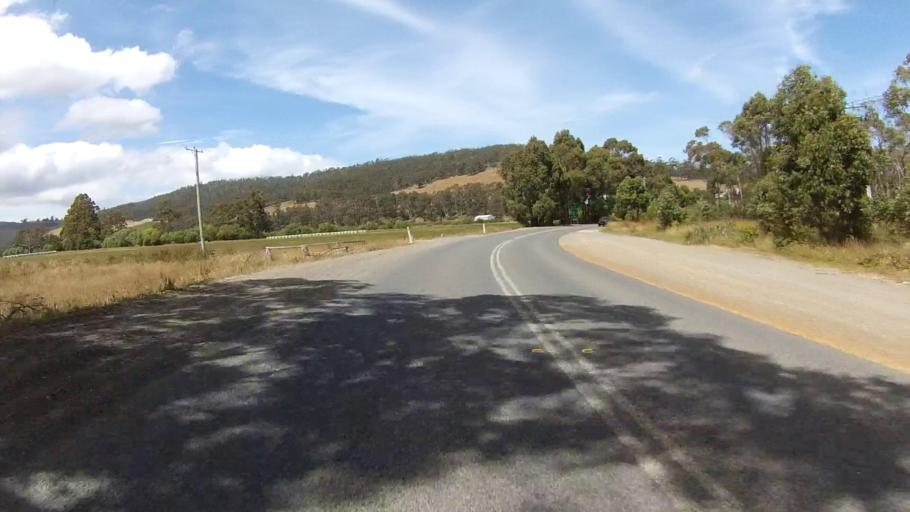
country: AU
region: Tasmania
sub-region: Huon Valley
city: Cygnet
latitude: -43.1685
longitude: 147.0954
